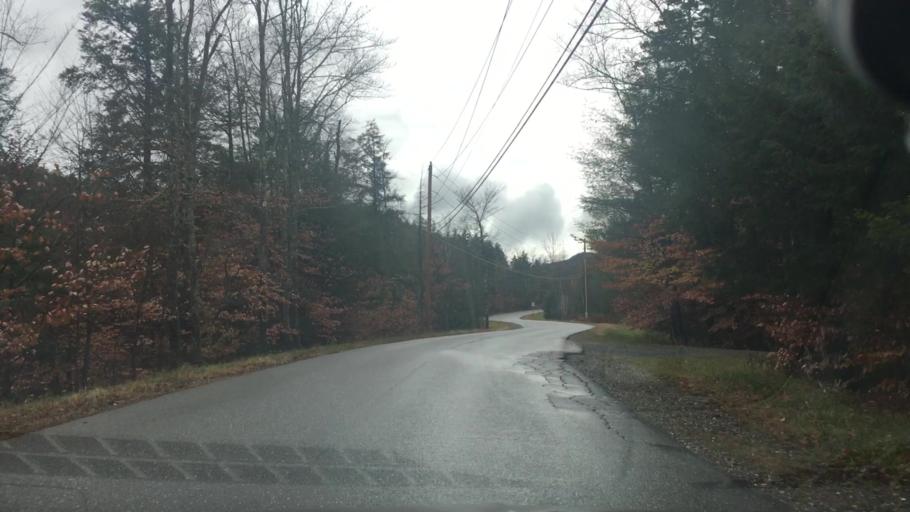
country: US
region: Vermont
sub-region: Lamoille County
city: Morristown
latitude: 44.5074
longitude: -72.7580
